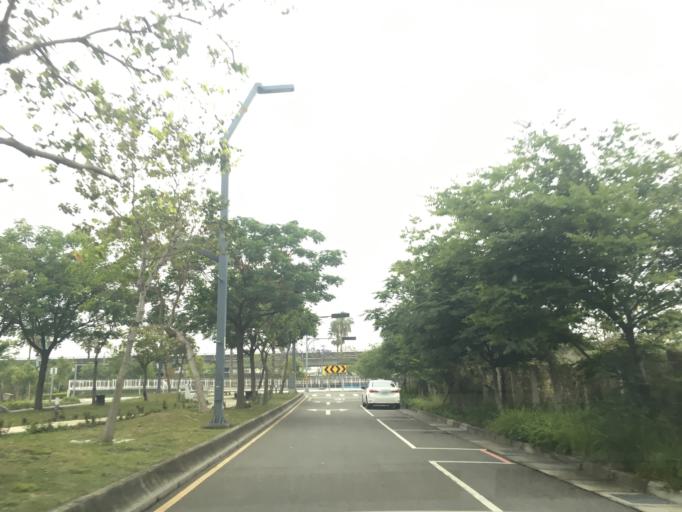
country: TW
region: Taiwan
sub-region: Taichung City
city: Taichung
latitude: 24.1943
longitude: 120.6468
